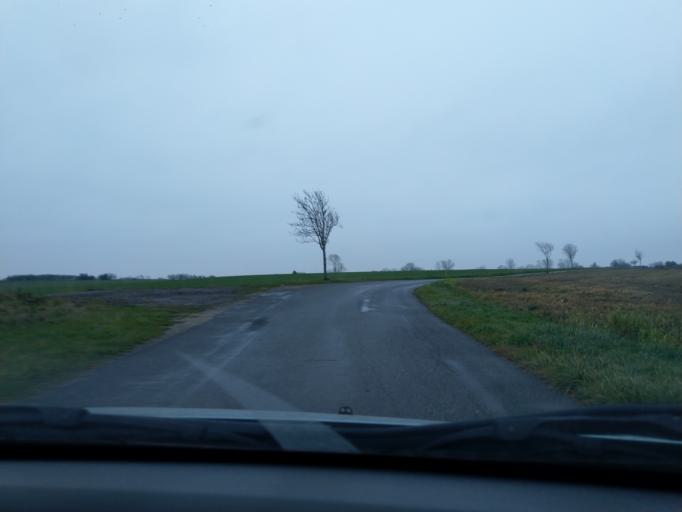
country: DK
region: Zealand
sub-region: Vordingborg Kommune
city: Praesto
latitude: 55.1136
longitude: 12.1134
